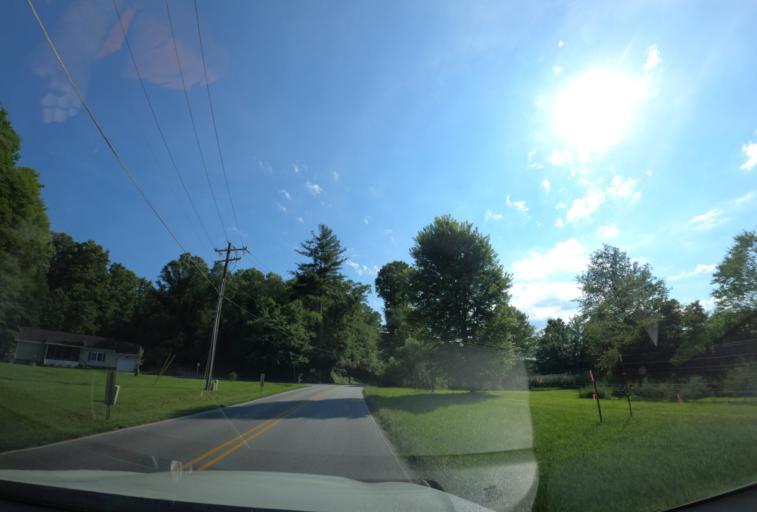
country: US
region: North Carolina
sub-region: Transylvania County
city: Brevard
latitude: 35.2533
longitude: -82.6725
